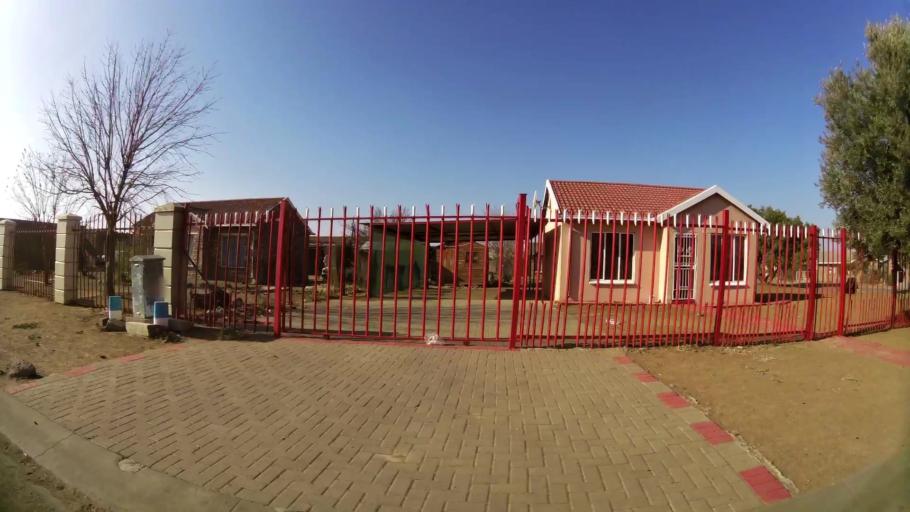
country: ZA
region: Orange Free State
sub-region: Mangaung Metropolitan Municipality
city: Bloemfontein
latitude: -29.1836
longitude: 26.1722
